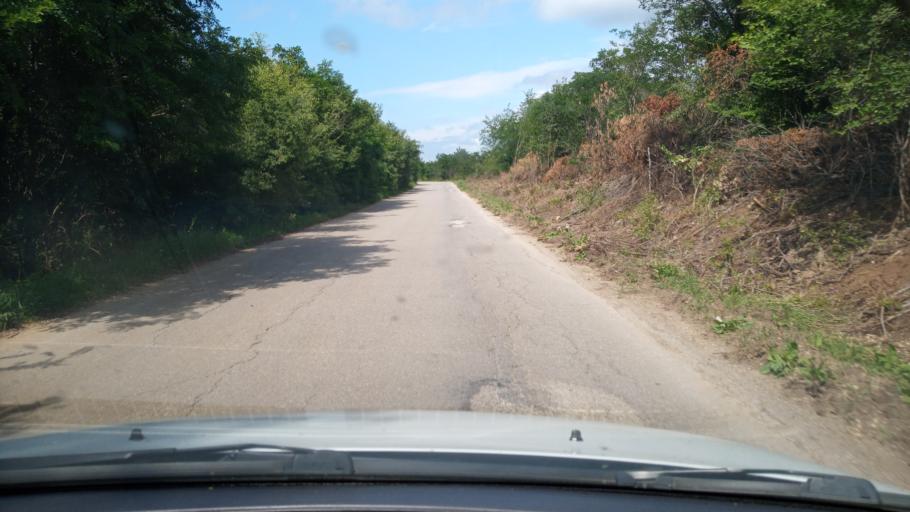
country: BG
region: Lovech
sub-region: Obshtina Lukovit
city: Lukovit
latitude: 43.2009
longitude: 24.1226
